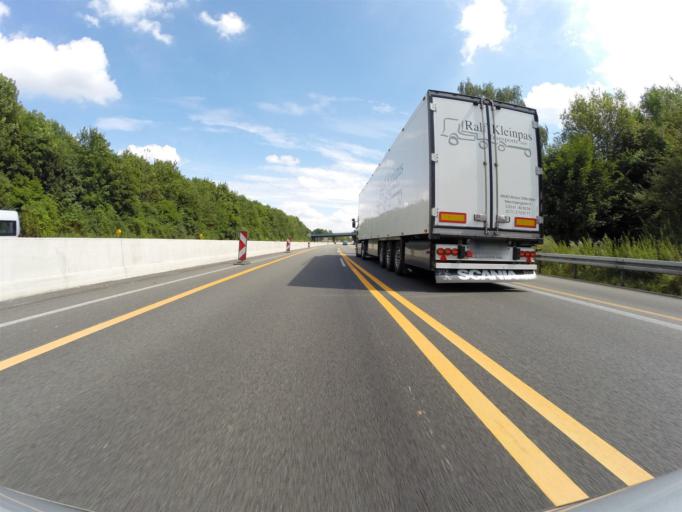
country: DE
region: North Rhine-Westphalia
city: Buende
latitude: 52.1889
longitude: 8.5783
